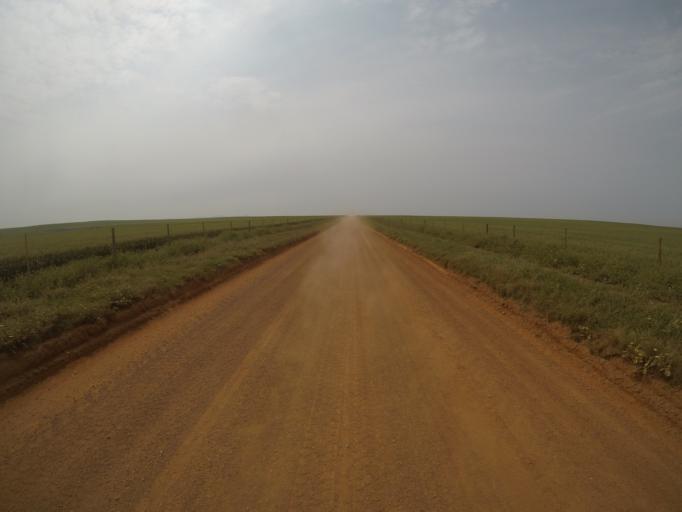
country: ZA
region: Western Cape
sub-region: City of Cape Town
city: Kraaifontein
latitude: -33.7232
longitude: 18.6704
